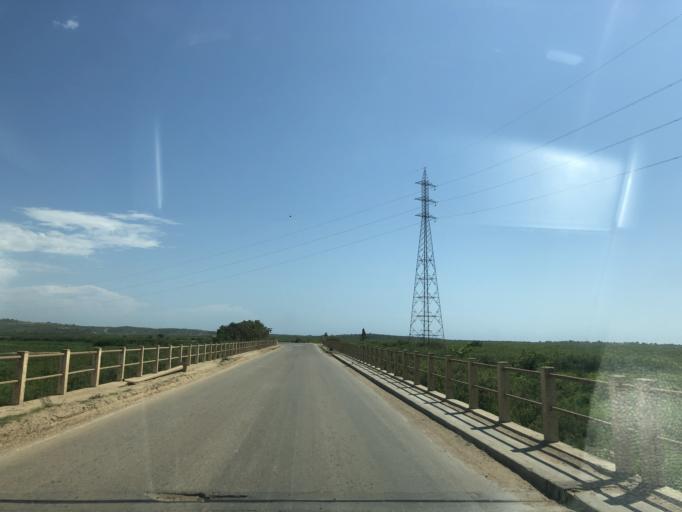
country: AO
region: Cuanza Sul
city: Sumbe
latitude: -10.8759
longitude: 13.8395
